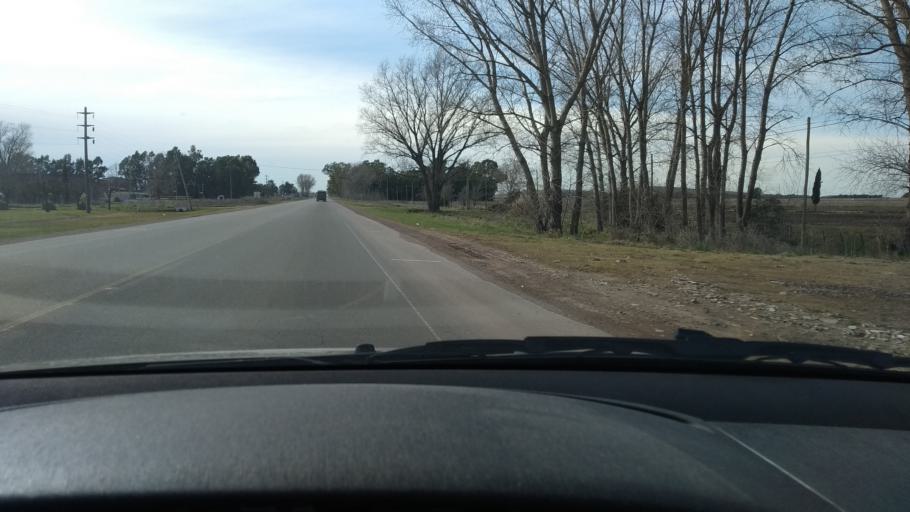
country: AR
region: Buenos Aires
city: Olavarria
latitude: -36.9507
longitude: -60.2477
